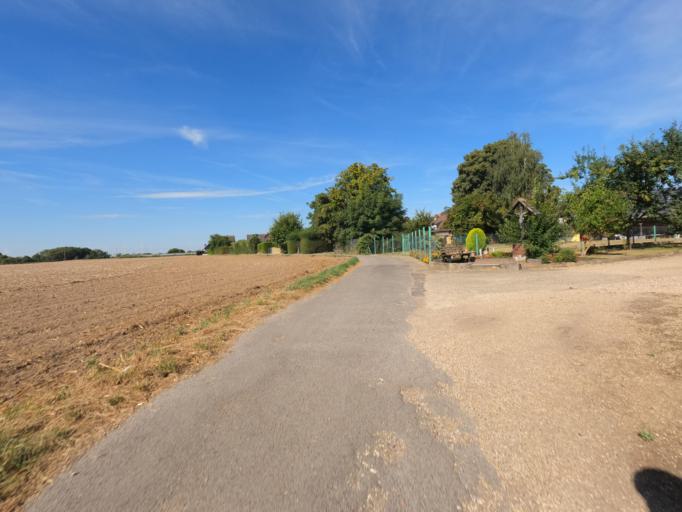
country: DE
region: North Rhine-Westphalia
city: Erkelenz
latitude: 51.0344
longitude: 6.3495
